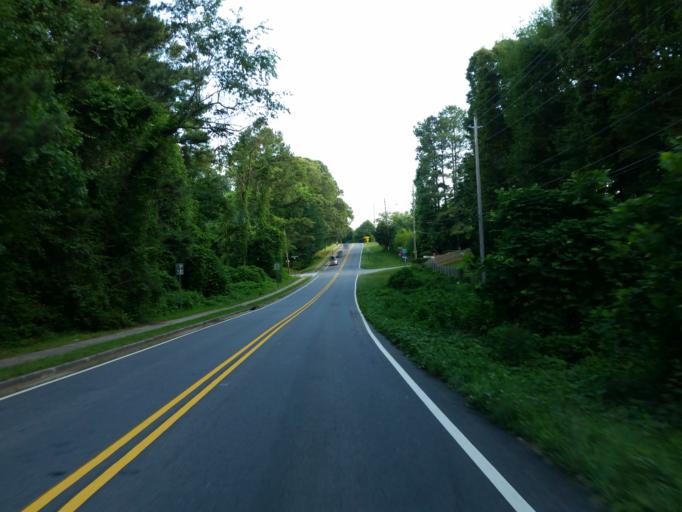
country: US
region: Georgia
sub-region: Cherokee County
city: Woodstock
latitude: 34.0505
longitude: -84.4849
